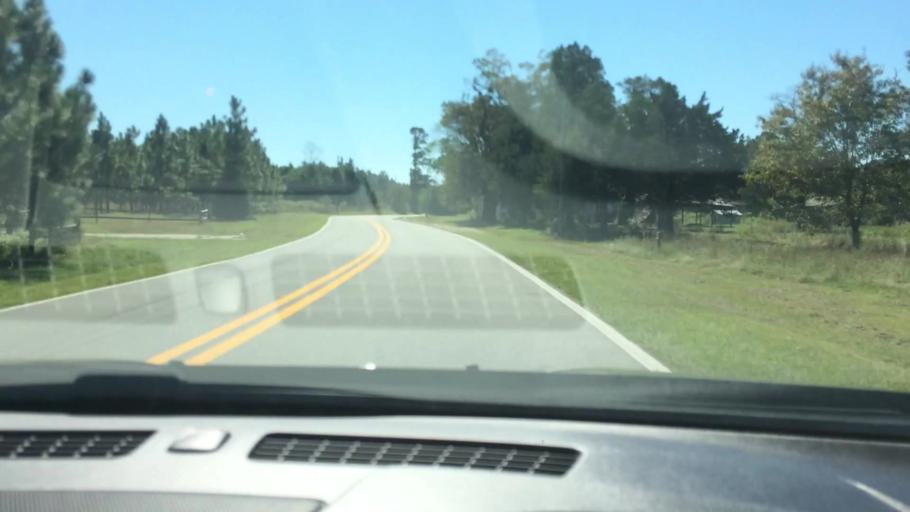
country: US
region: North Carolina
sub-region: Craven County
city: Vanceboro
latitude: 35.3289
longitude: -77.2983
